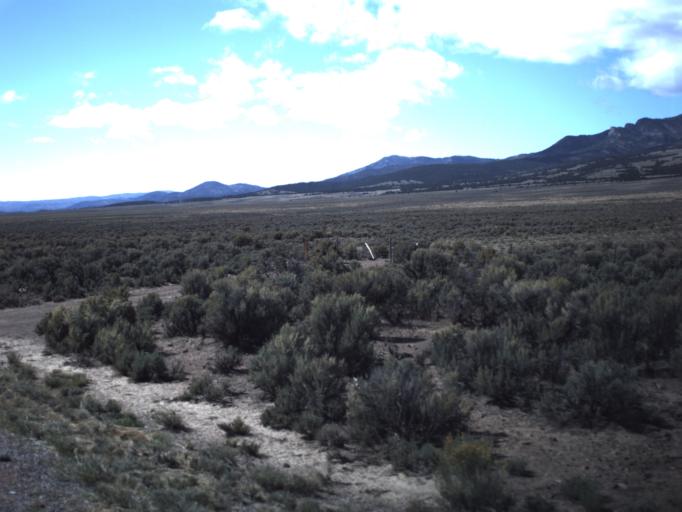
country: US
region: Utah
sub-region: Wayne County
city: Loa
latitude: 38.4020
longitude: -111.9291
